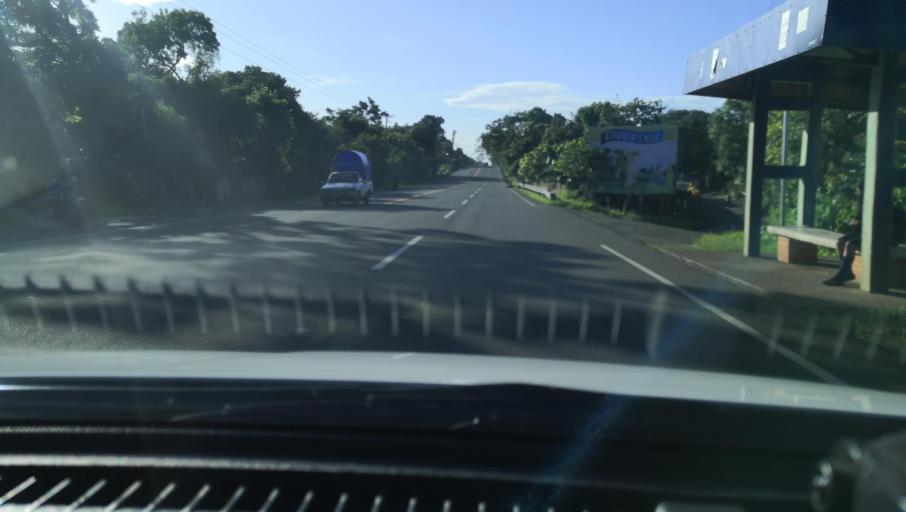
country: NI
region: Carazo
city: La Paz de Oriente
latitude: 11.8202
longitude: -86.1516
